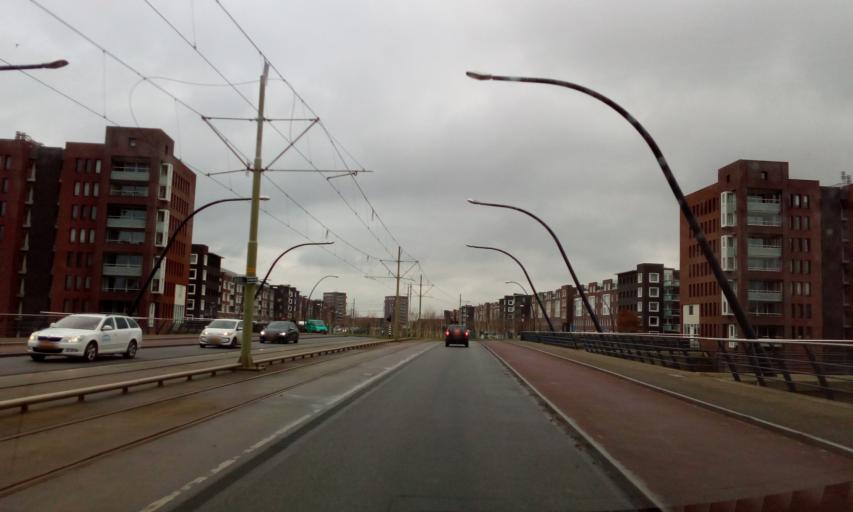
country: NL
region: South Holland
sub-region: Gemeente Rijswijk
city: Rijswijk
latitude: 52.0244
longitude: 4.2920
